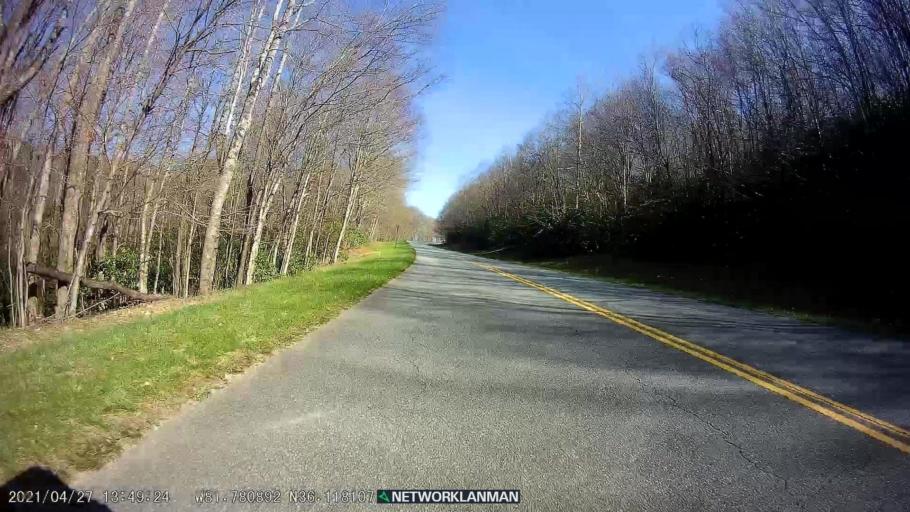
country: US
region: North Carolina
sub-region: Watauga County
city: Foscoe
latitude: 36.1182
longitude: -81.7811
